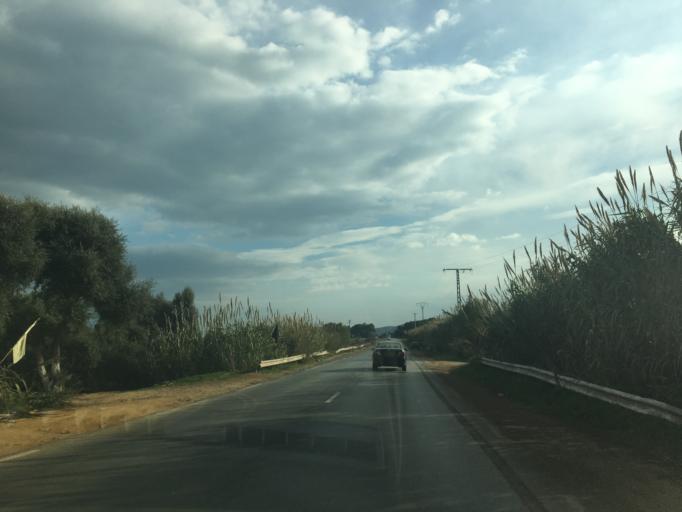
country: DZ
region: Tipaza
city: Tipasa
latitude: 36.5895
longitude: 2.5075
